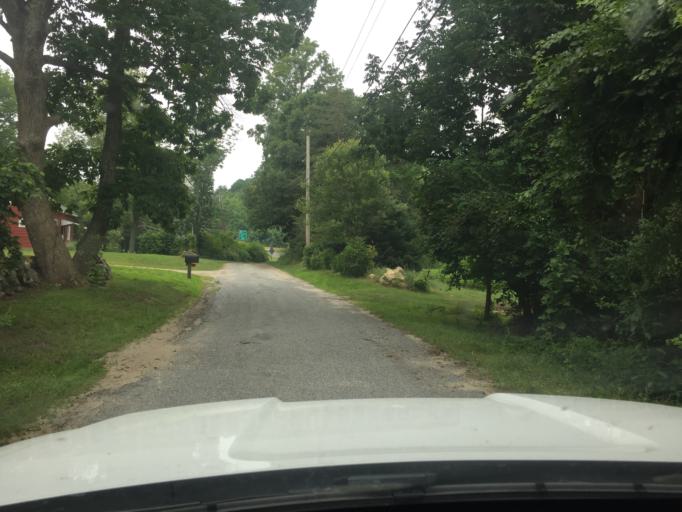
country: US
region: Connecticut
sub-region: New London County
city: Montville Center
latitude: 41.5726
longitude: -72.2068
